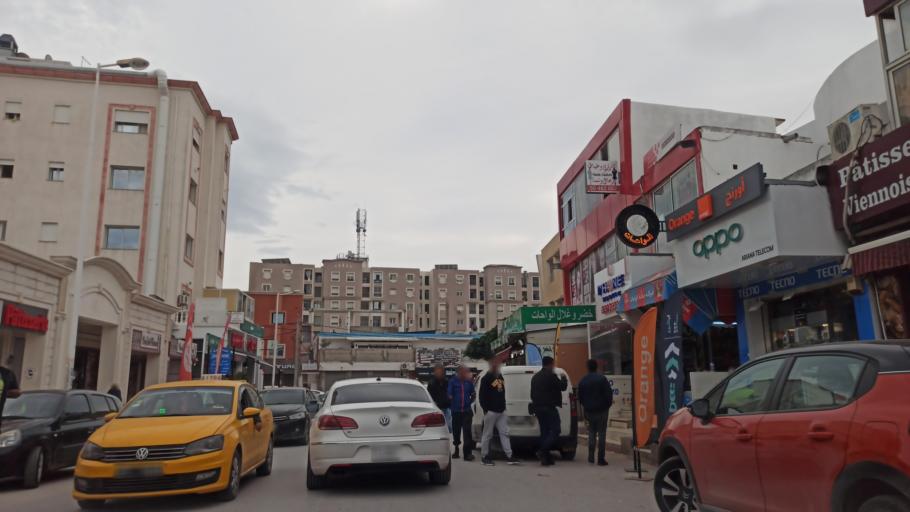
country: TN
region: Tunis
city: La Goulette
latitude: 36.8581
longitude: 10.2663
